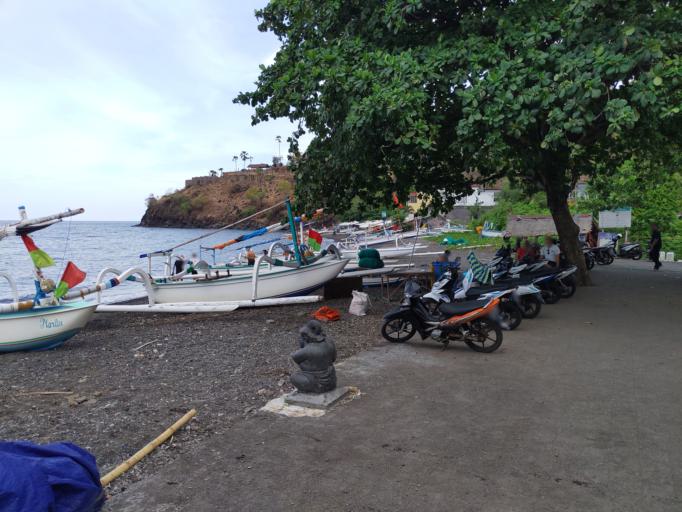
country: ID
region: Bali
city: Biaslantang Kaler
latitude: -8.3384
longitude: 115.6598
